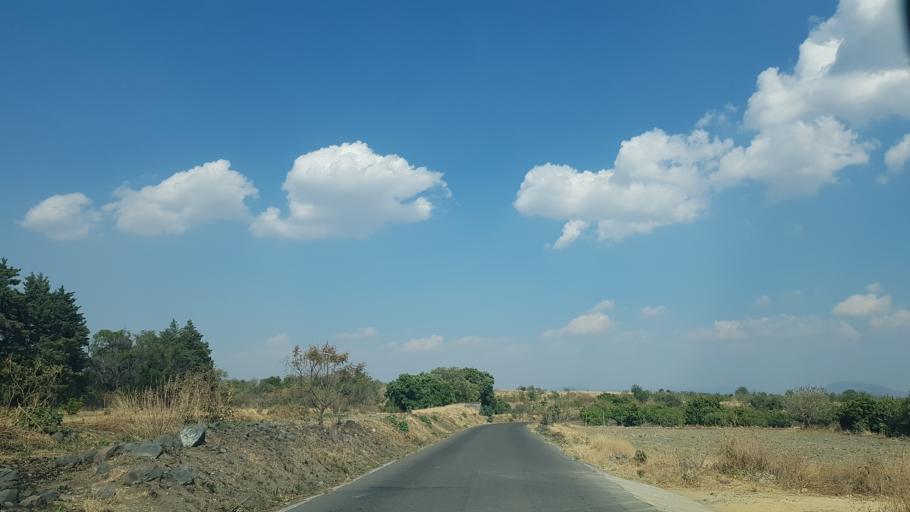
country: MX
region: Puebla
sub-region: Atlixco
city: Colonia Agricola de Ocotepec (Colonia San Jose)
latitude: 18.9211
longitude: -98.5353
